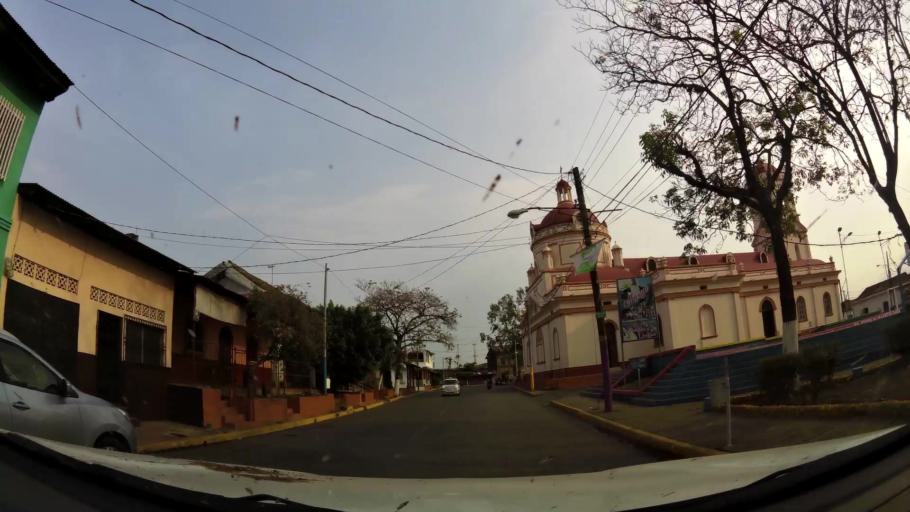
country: NI
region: Masaya
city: Masaya
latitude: 11.9794
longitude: -86.0972
